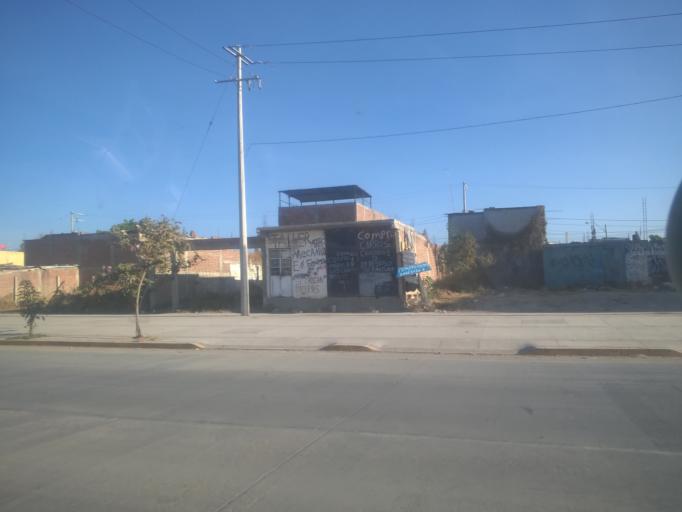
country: MX
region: Guanajuato
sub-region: Leon
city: San Jose de Duran (Los Troncoso)
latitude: 21.0660
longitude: -101.6341
